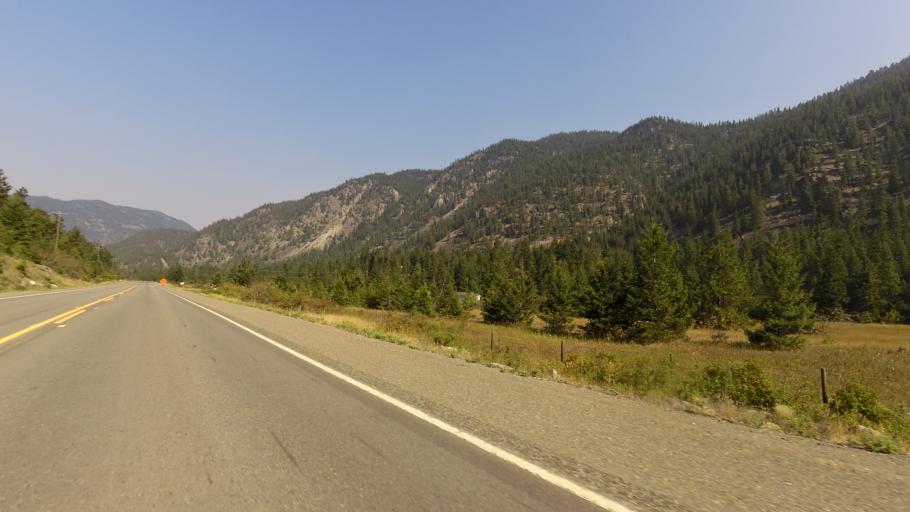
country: CA
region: British Columbia
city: Princeton
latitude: 49.3955
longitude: -120.2142
